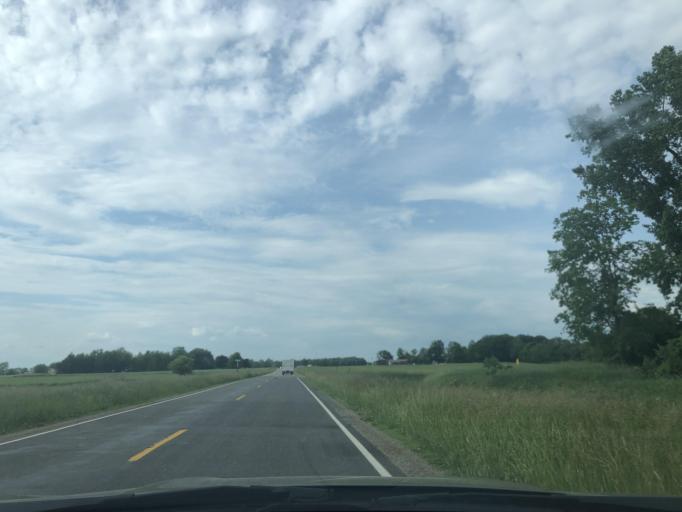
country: US
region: Michigan
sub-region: Clinton County
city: Saint Johns
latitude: 42.9852
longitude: -84.4838
